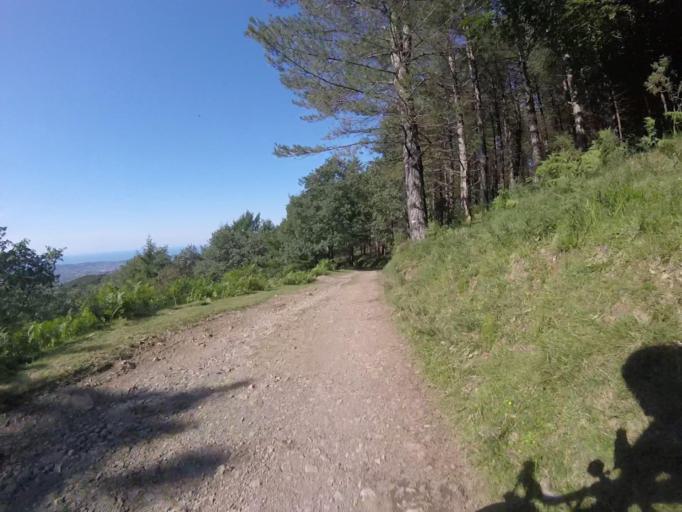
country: ES
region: Basque Country
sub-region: Provincia de Guipuzcoa
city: Irun
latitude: 43.2999
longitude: -1.7834
